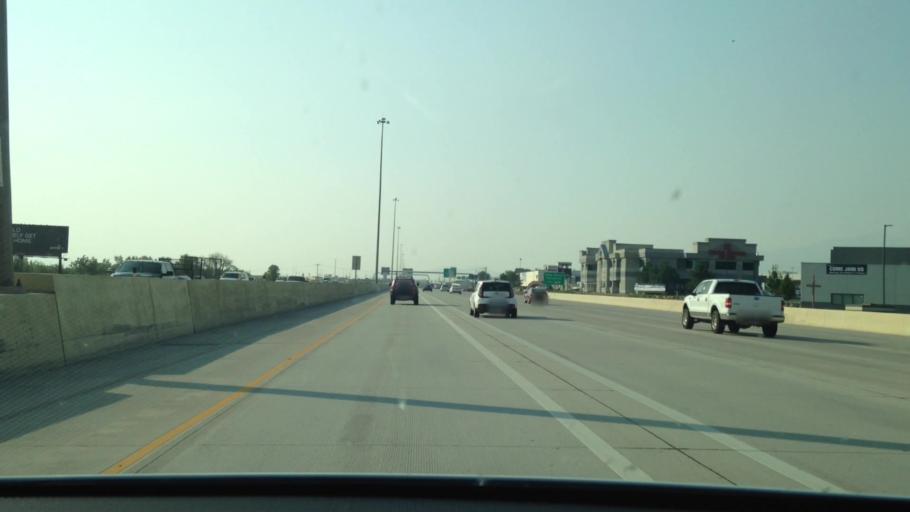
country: US
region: Utah
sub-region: Utah County
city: Orem
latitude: 40.2679
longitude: -111.7125
